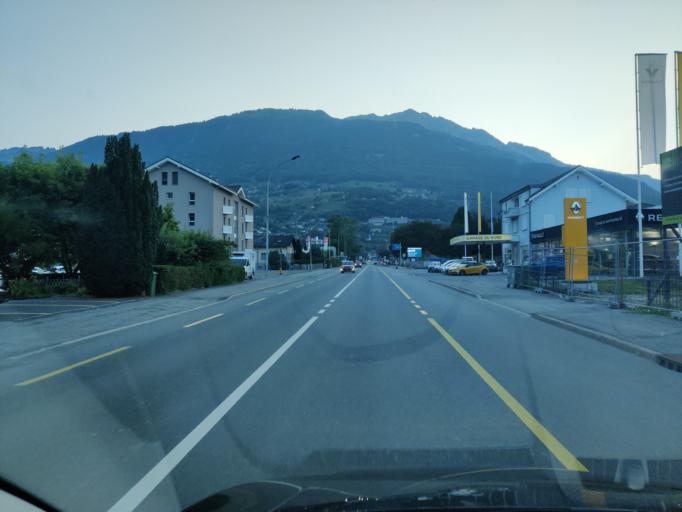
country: CH
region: Valais
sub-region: Monthey District
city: Monthey
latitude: 46.2480
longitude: 6.9582
